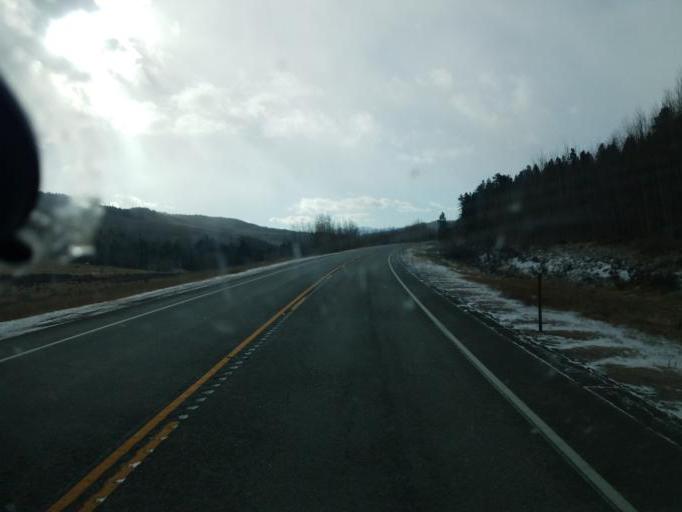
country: US
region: Colorado
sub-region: Summit County
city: Breckenridge
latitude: 39.4115
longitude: -105.7573
